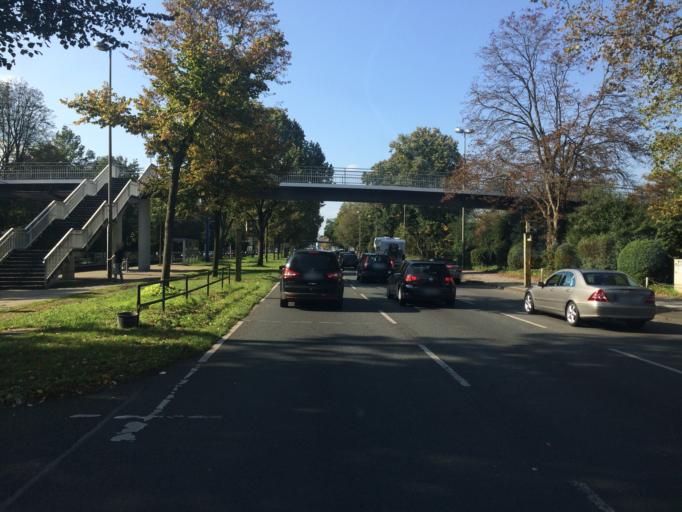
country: DE
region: North Rhine-Westphalia
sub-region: Regierungsbezirk Arnsberg
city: Dortmund
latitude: 51.5039
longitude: 7.5079
